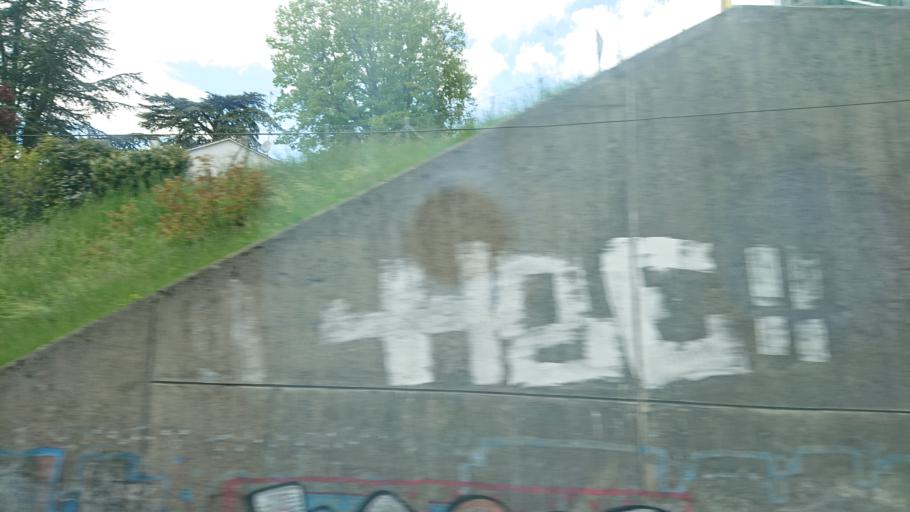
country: CH
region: Vaud
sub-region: Nyon District
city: Nyon
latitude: 46.3807
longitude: 6.2314
